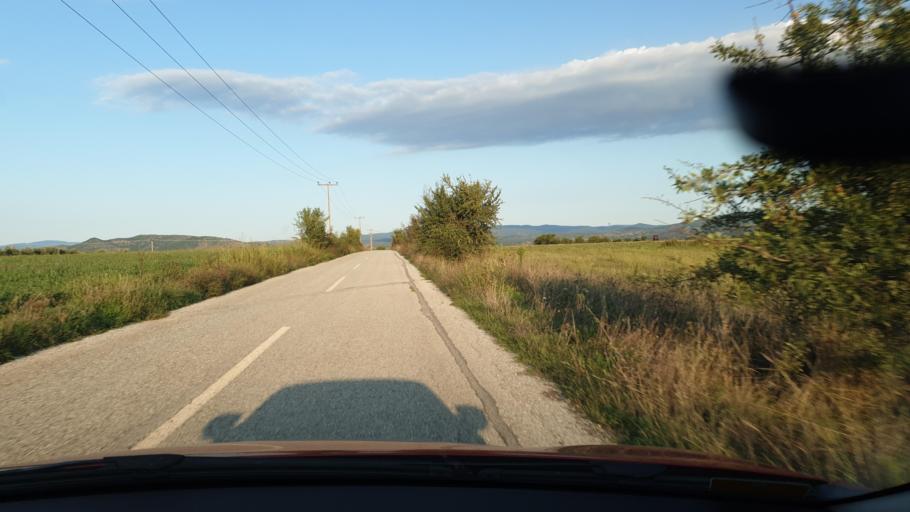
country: GR
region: Central Macedonia
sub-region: Nomos Thessalonikis
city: Nea Apollonia
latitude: 40.5558
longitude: 23.4569
